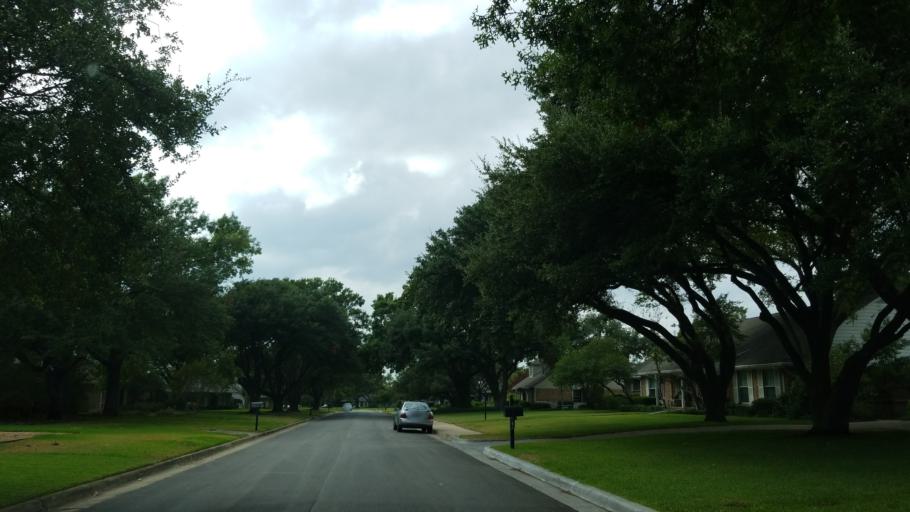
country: US
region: Texas
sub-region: Dallas County
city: Addison
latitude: 32.9439
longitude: -96.7823
